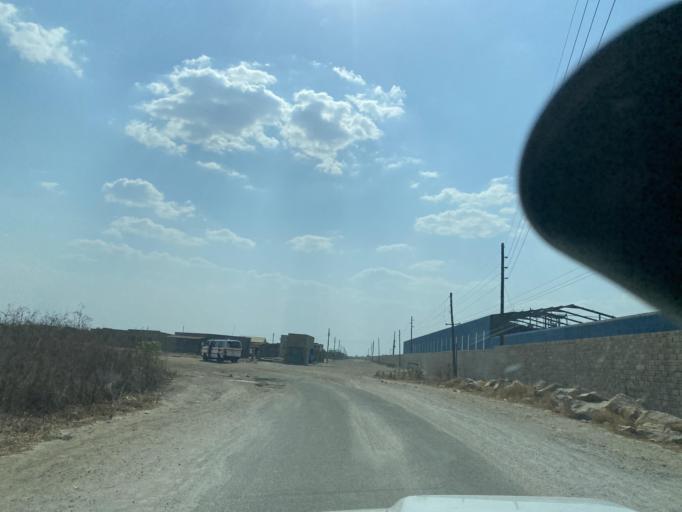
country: ZM
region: Lusaka
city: Lusaka
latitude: -15.3580
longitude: 28.0976
